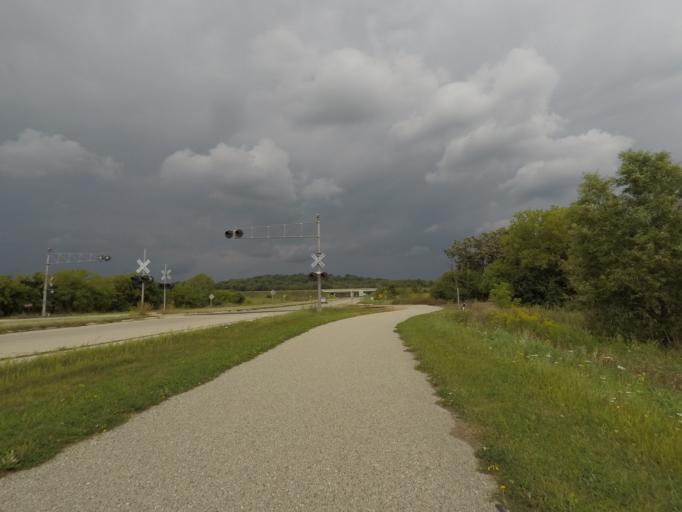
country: US
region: Wisconsin
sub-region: Jefferson County
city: Fort Atkinson
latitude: 42.9511
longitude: -88.8285
